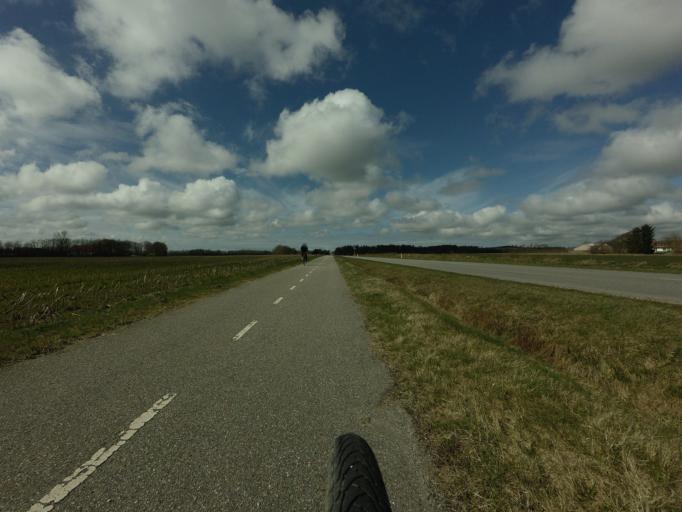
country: DK
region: North Denmark
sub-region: Hjorring Kommune
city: Vra
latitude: 57.3545
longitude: 9.8937
